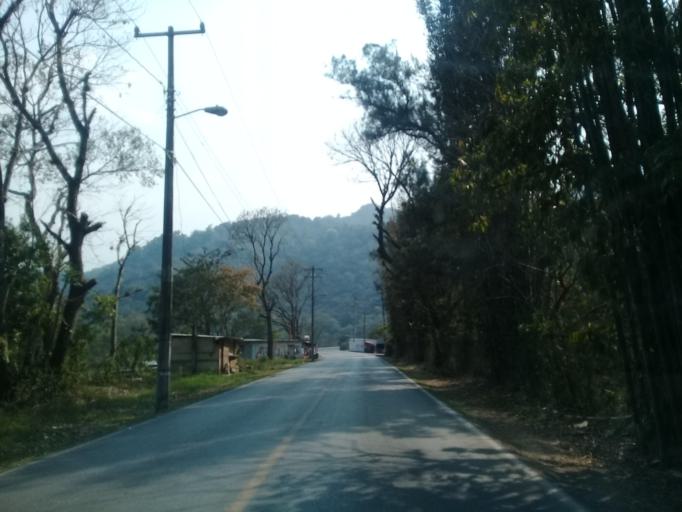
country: MX
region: Veracruz
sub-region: Ixtaczoquitlan
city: Campo Chico
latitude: 18.8349
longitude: -97.0235
